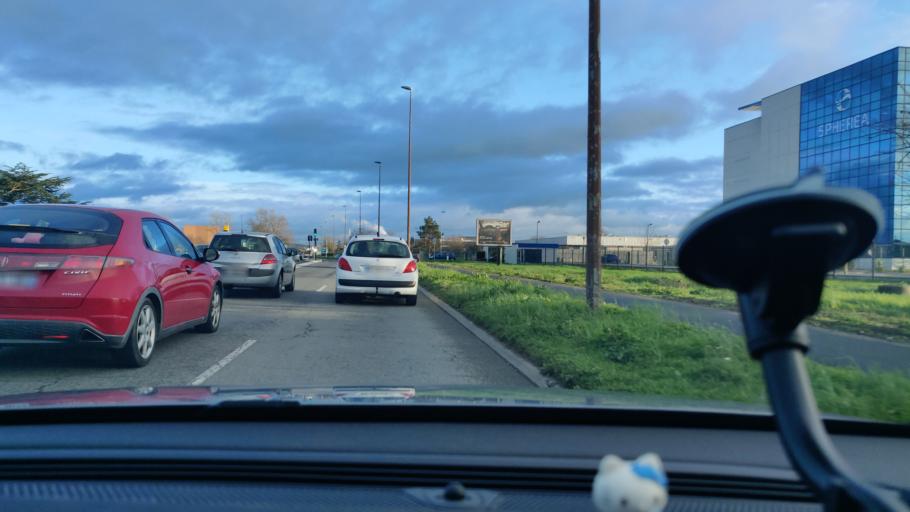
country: FR
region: Midi-Pyrenees
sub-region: Departement de la Haute-Garonne
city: Cugnaux
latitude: 43.5668
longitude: 1.3784
